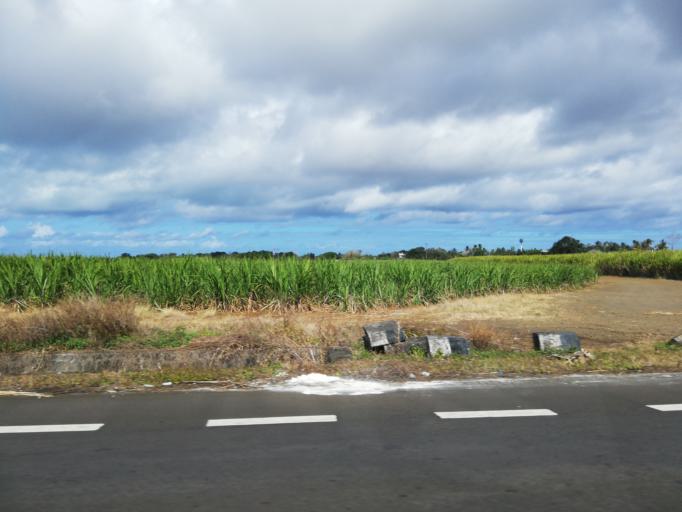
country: MU
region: Grand Port
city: Mahebourg
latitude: -20.4037
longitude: 57.6772
